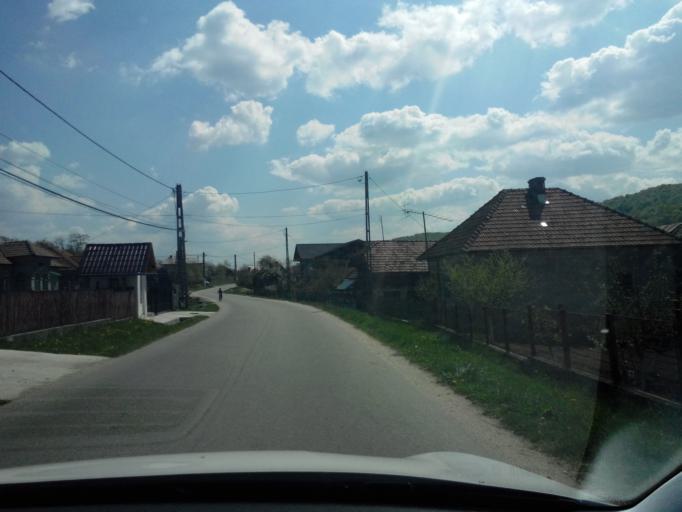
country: RO
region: Arges
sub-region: Comuna Baiculesti
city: Tutana
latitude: 45.0392
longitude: 24.6546
